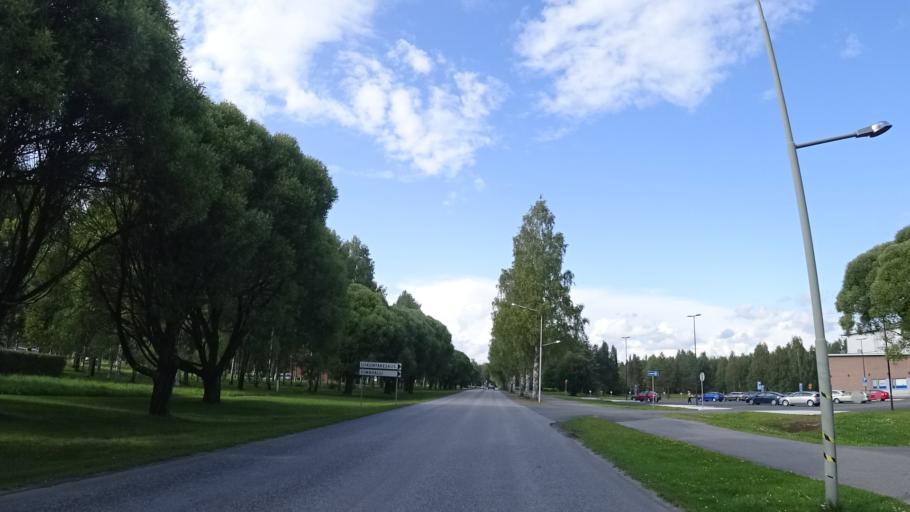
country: FI
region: North Karelia
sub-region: Pielisen Karjala
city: Lieksa
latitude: 63.3247
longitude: 30.0226
